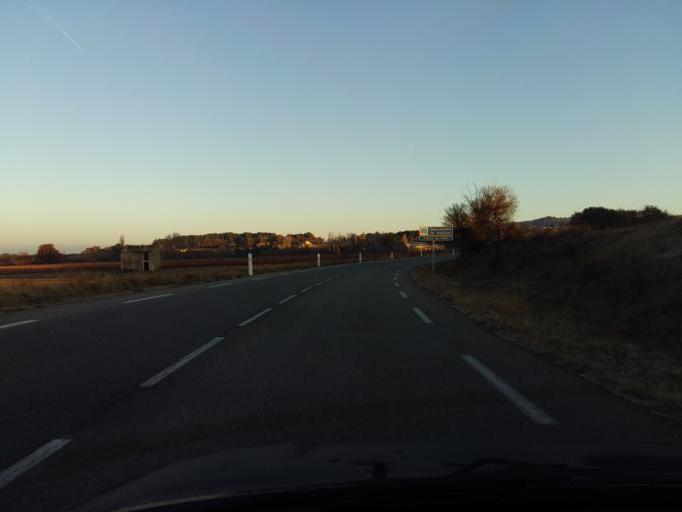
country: FR
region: Provence-Alpes-Cote d'Azur
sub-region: Departement du Vaucluse
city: Visan
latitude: 44.3049
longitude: 4.9439
